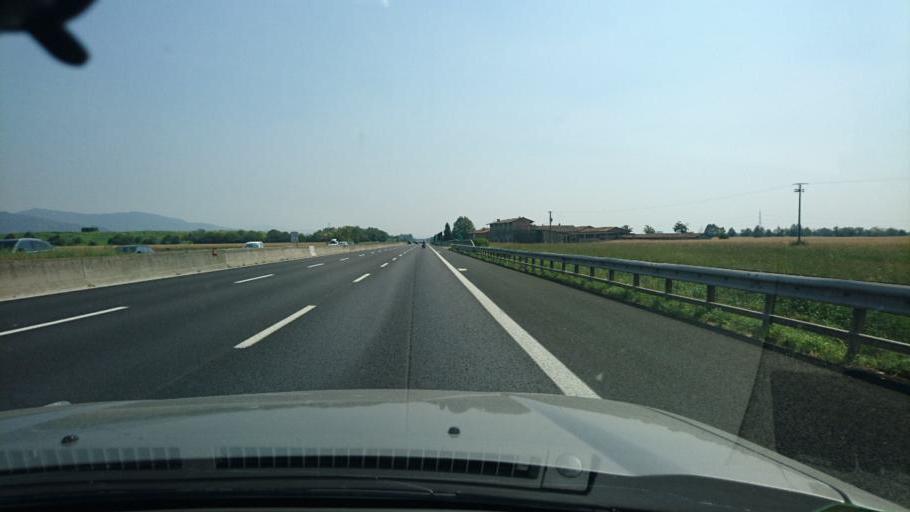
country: IT
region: Lombardy
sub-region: Provincia di Bergamo
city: Bagnatica
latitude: 45.6476
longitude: 9.7884
